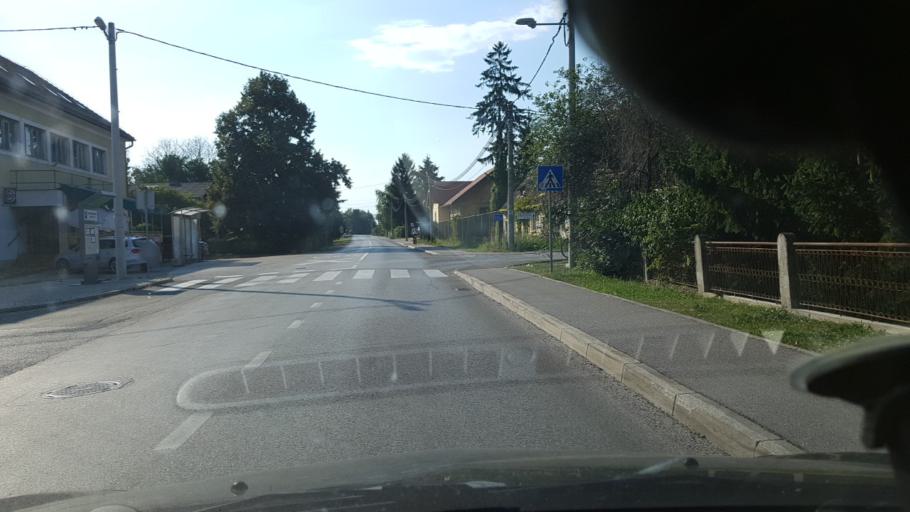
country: HR
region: Zagrebacka
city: Bregana
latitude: 45.8878
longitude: 15.6955
